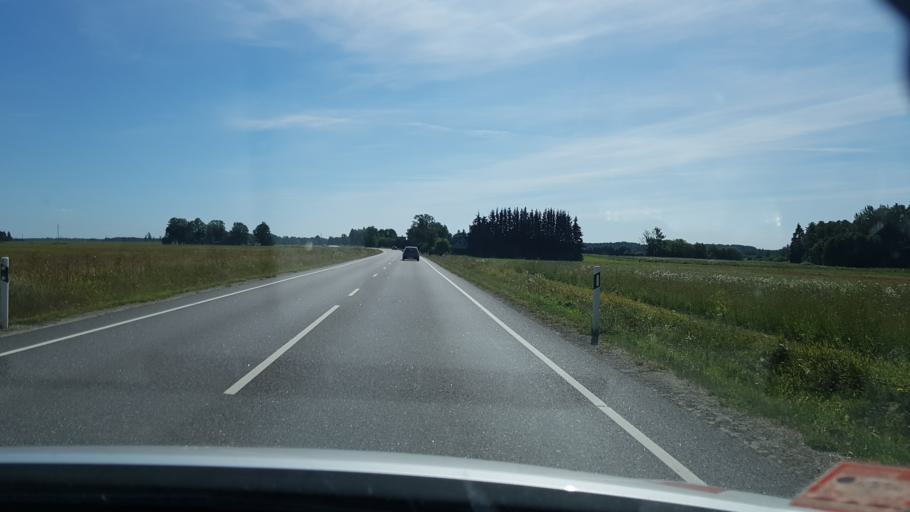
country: EE
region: Tartu
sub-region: Tartu linn
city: Tartu
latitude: 58.4224
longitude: 26.8628
